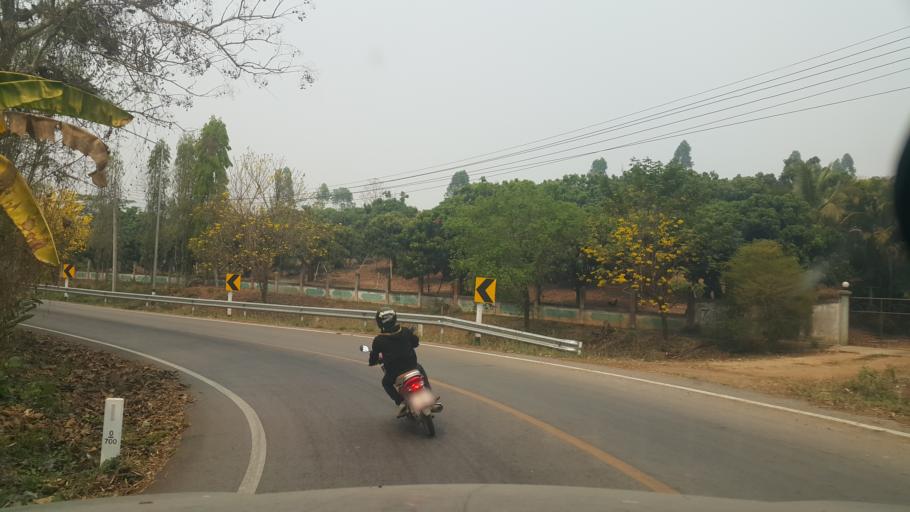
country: TH
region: Lamphun
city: Mae Tha
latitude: 18.4653
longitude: 99.1778
